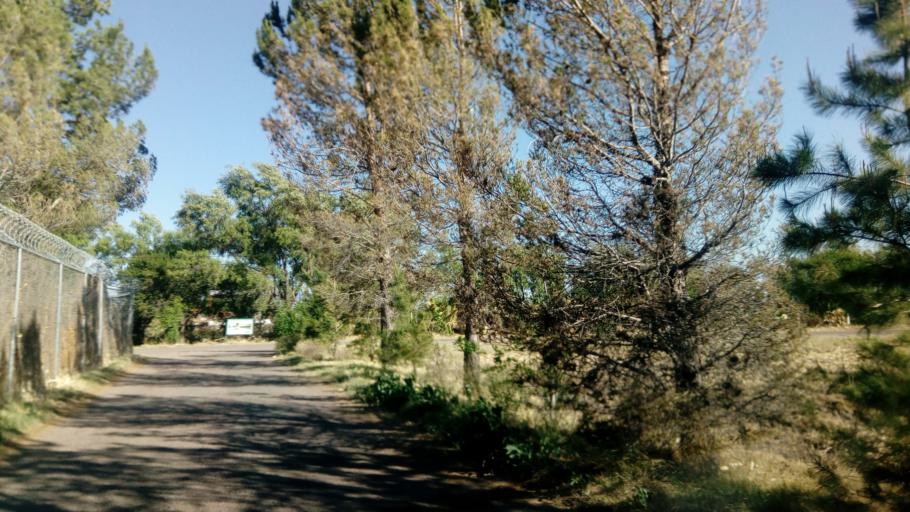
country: MX
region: Durango
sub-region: Durango
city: Jose Refugio Salcido
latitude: 24.0093
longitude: -104.5486
